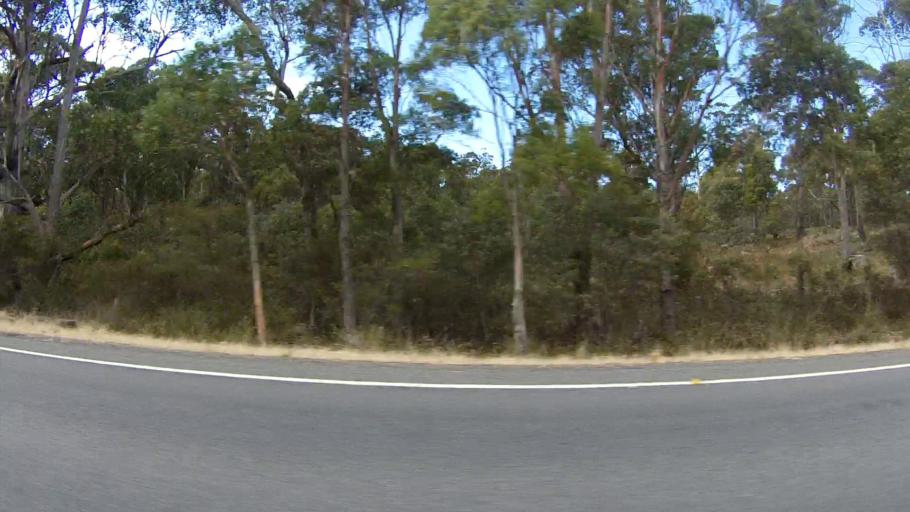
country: AU
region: Tasmania
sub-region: Sorell
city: Sorell
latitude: -42.6234
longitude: 147.6324
